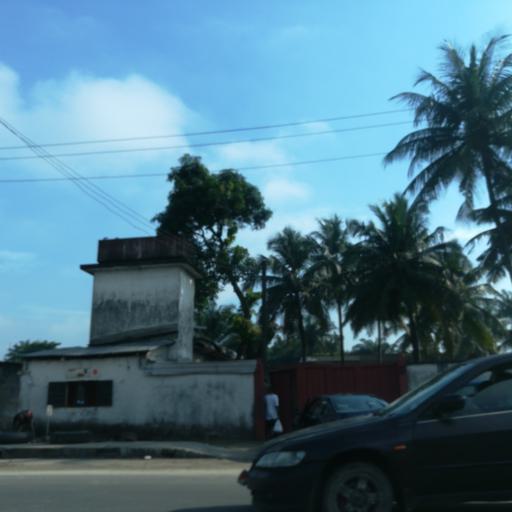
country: NG
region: Rivers
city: Port Harcourt
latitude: 4.8014
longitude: 7.0221
